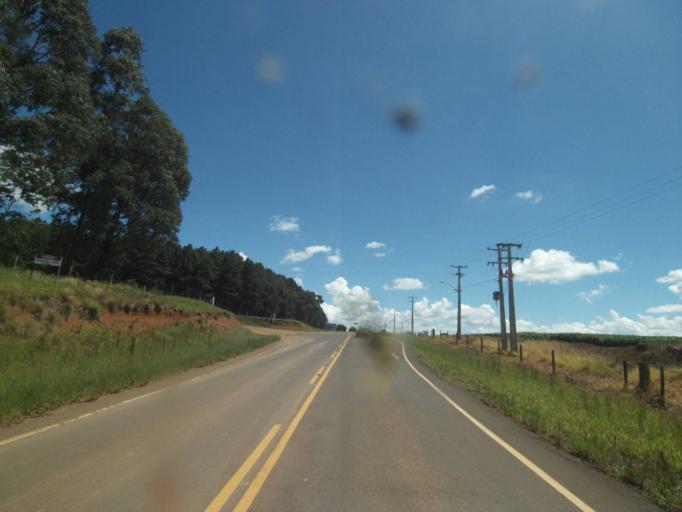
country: BR
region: Parana
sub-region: Pinhao
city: Pinhao
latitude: -25.8327
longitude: -52.0213
